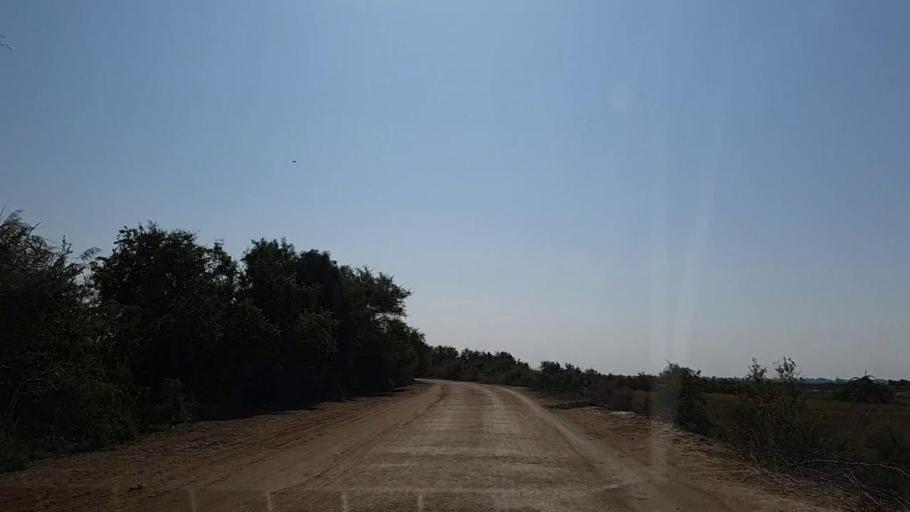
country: PK
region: Sindh
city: Chuhar Jamali
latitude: 24.5144
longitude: 68.0958
